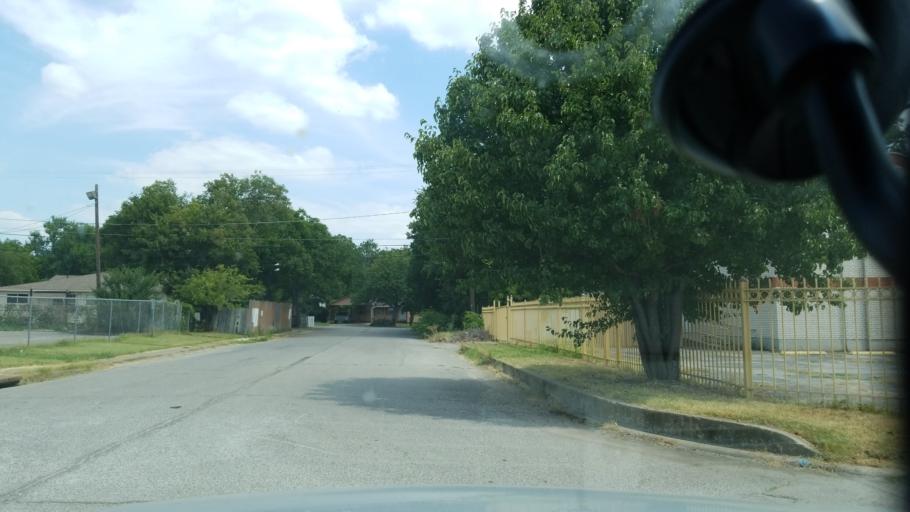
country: US
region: Texas
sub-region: Dallas County
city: Grand Prairie
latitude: 32.7525
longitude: -96.9758
